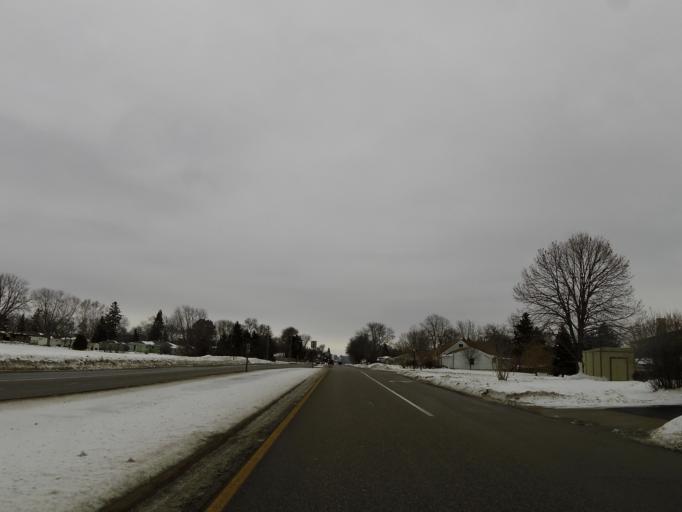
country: US
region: Minnesota
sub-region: Dakota County
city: Inver Grove Heights
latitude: 44.8480
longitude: -93.0295
